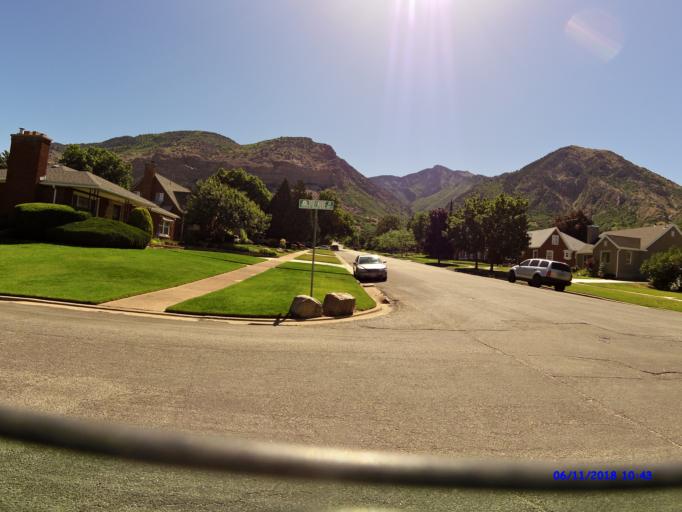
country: US
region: Utah
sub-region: Weber County
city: Ogden
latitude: 41.2182
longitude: -111.9373
